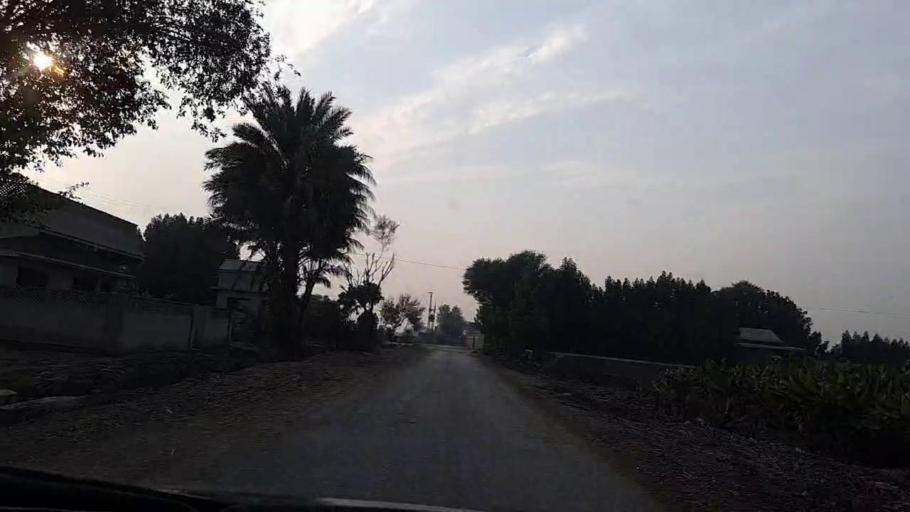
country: PK
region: Sindh
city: Nawabshah
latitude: 26.2834
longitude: 68.3220
